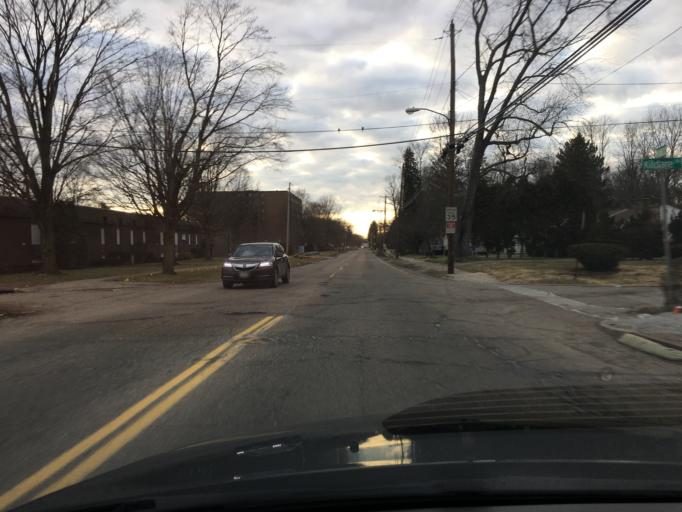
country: US
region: Ohio
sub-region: Summit County
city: Fairlawn
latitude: 41.0998
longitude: -81.5726
